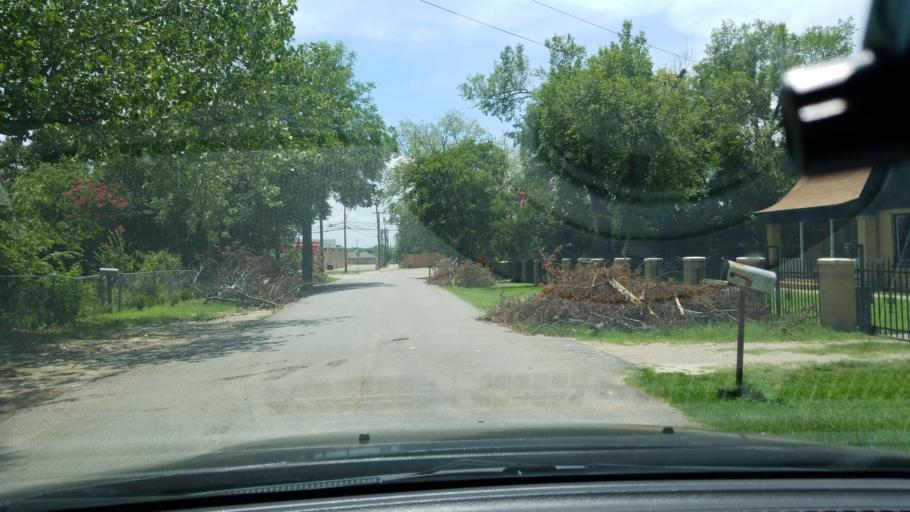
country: US
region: Texas
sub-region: Dallas County
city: Balch Springs
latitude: 32.7495
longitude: -96.6505
